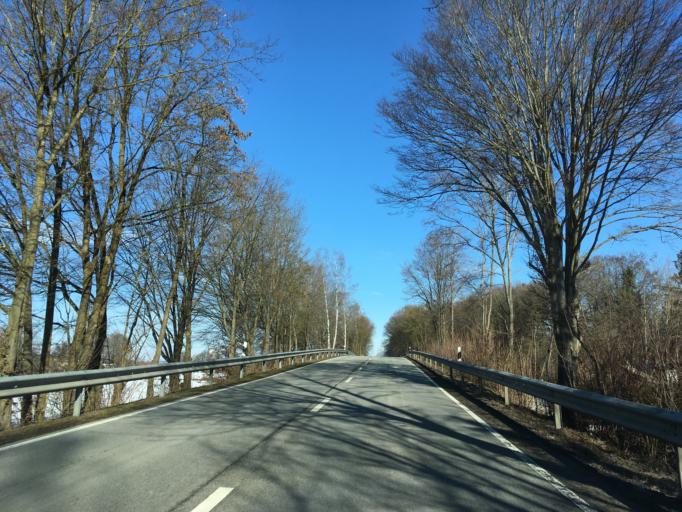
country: DE
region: Bavaria
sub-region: Upper Bavaria
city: Edling
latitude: 48.0602
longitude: 12.1570
